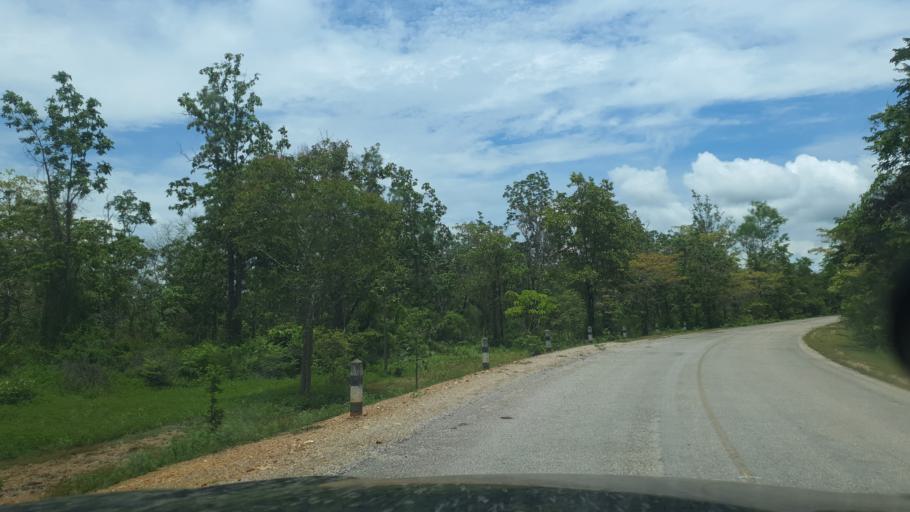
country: TH
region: Lampang
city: Soem Ngam
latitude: 18.0523
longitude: 99.3651
